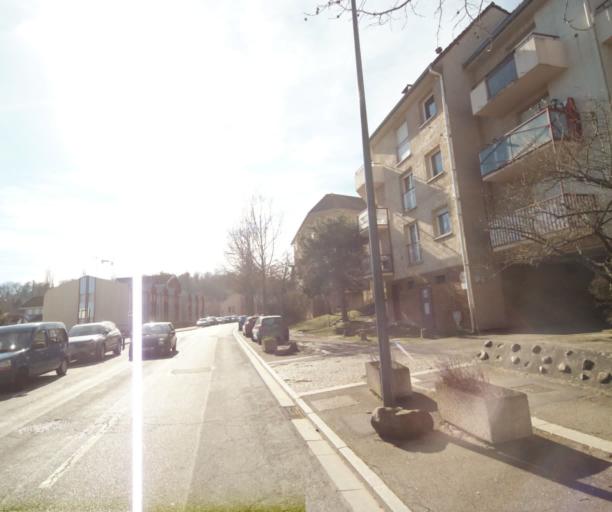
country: FR
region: Lorraine
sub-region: Departement de Meurthe-et-Moselle
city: Villers-les-Nancy
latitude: 48.6708
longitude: 6.1494
